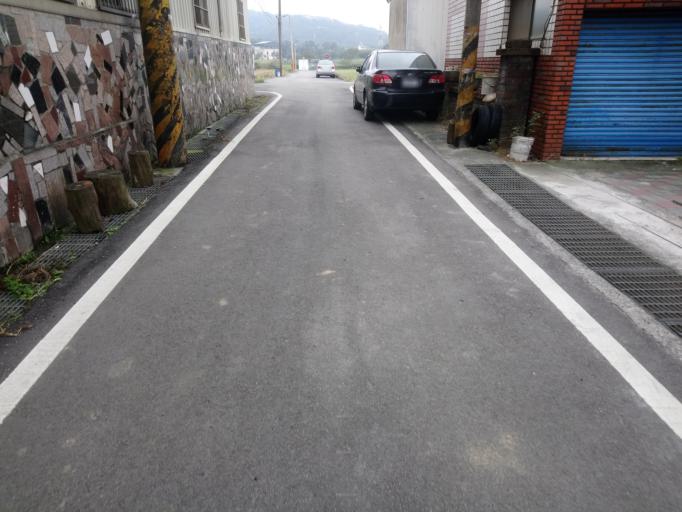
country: TW
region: Taiwan
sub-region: Hsinchu
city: Zhubei
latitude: 24.8880
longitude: 121.0779
